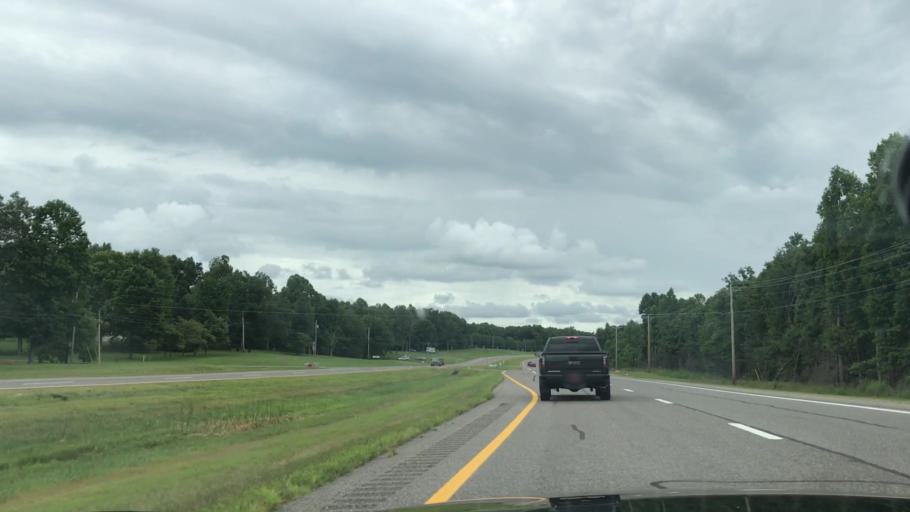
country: US
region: Tennessee
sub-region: Fentress County
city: Jamestown
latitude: 36.3743
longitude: -84.9442
